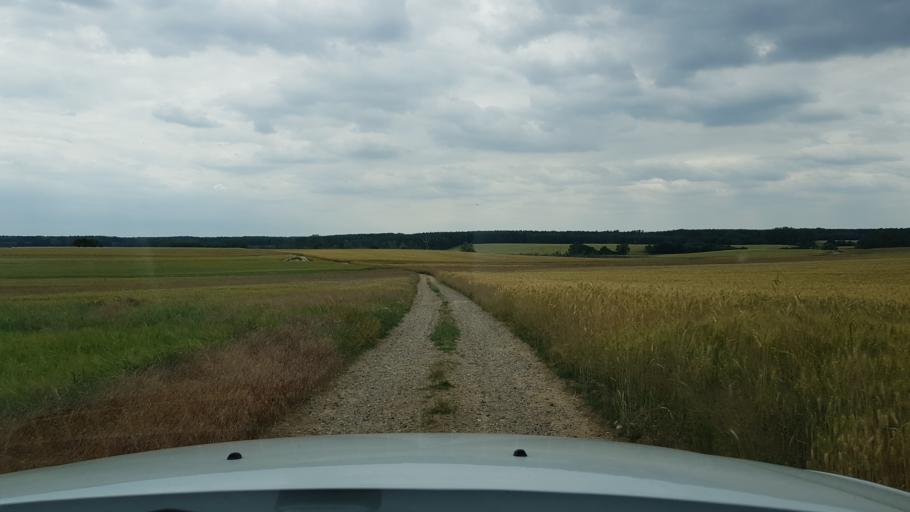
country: PL
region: West Pomeranian Voivodeship
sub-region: Powiat mysliborski
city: Boleszkowice
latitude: 52.6797
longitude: 14.6307
